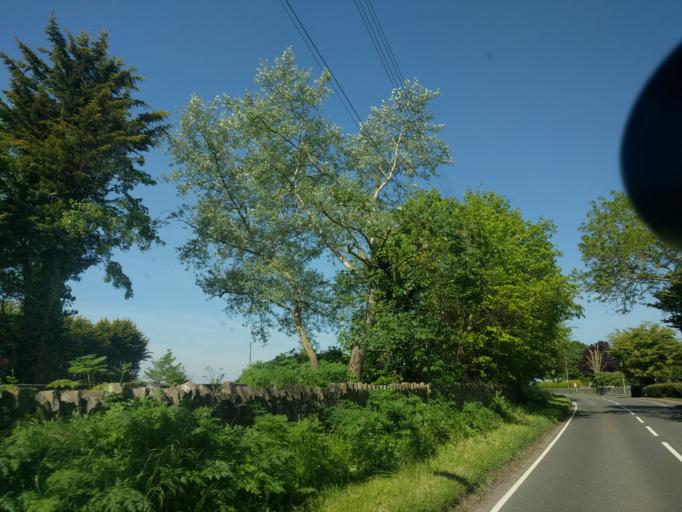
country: GB
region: England
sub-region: Somerset
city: Langport
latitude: 51.0337
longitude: -2.7744
